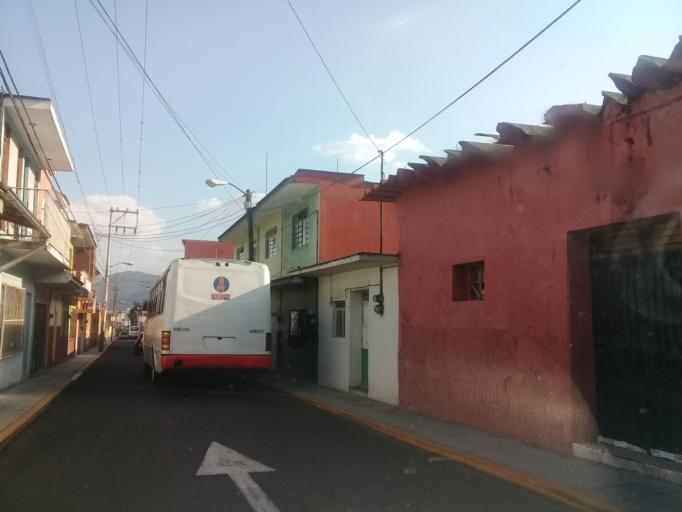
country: MX
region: Veracruz
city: Orizaba
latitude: 18.8506
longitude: -97.1116
